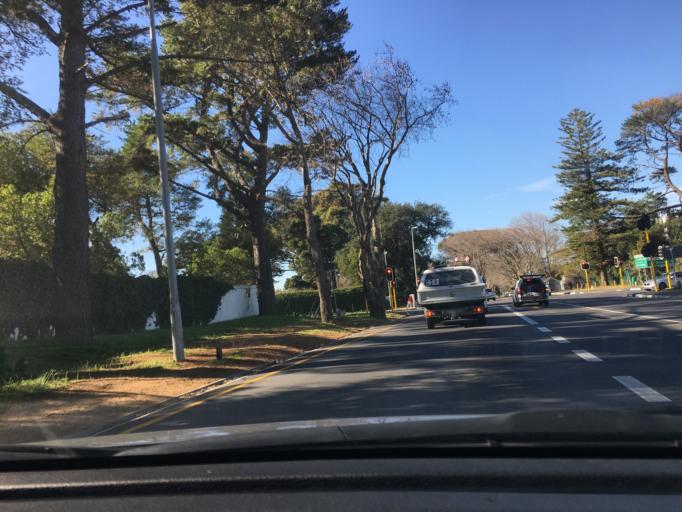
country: ZA
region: Western Cape
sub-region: City of Cape Town
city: Constantia
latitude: -34.0218
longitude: 18.4380
